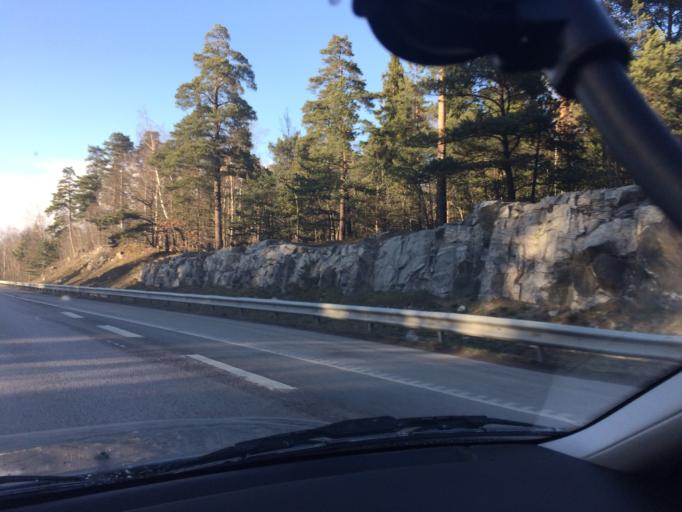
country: SE
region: Stockholm
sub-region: Jarfalla Kommun
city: Jakobsberg
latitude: 59.4270
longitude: 17.8503
